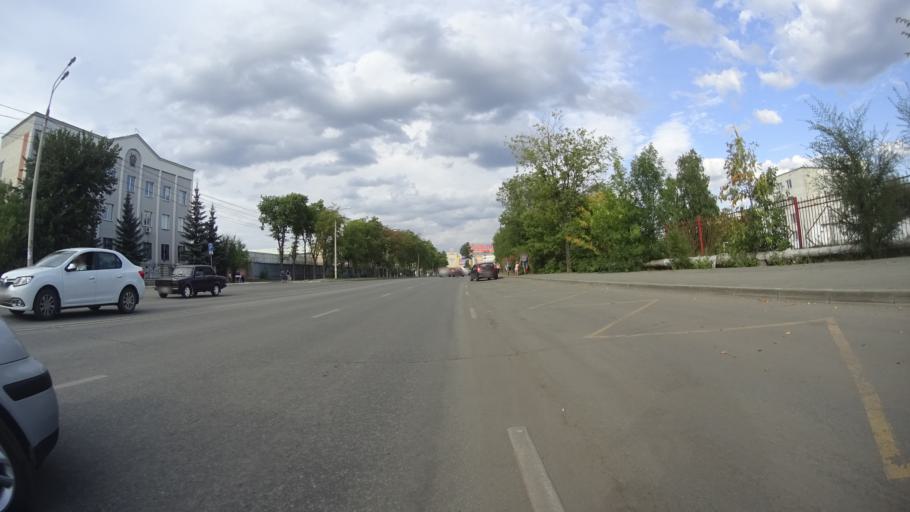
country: RU
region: Chelyabinsk
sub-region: Gorod Chelyabinsk
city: Chelyabinsk
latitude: 55.2024
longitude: 61.3218
